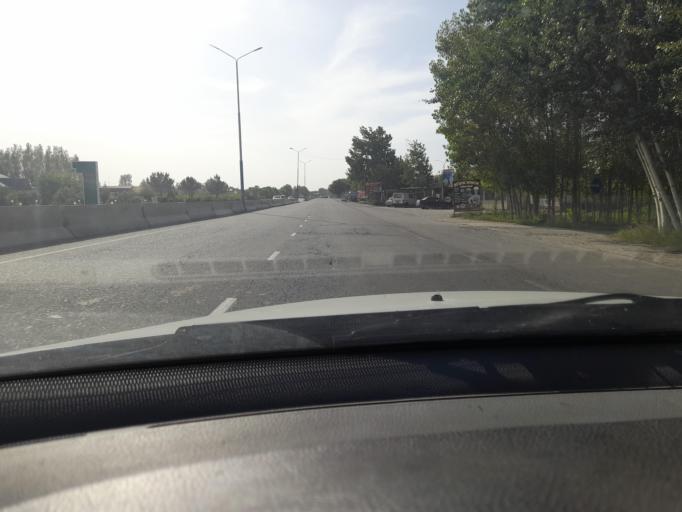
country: UZ
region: Samarqand
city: Kattaqo'rg'on
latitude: 39.9254
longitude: 66.2230
